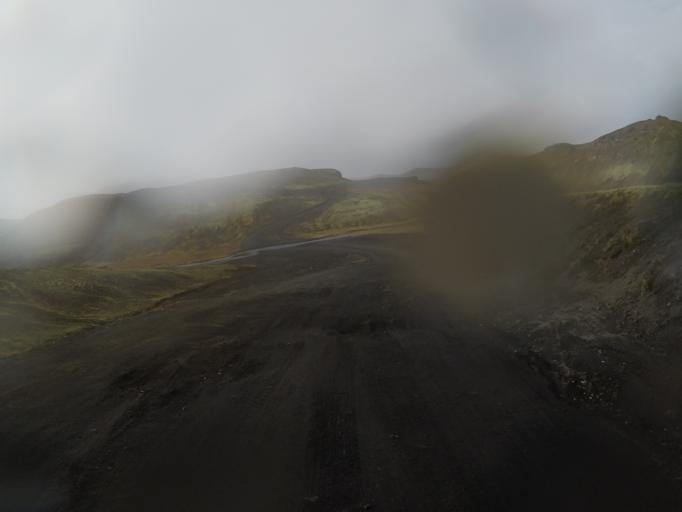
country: IS
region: South
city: Vestmannaeyjar
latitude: 63.9798
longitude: -18.8777
